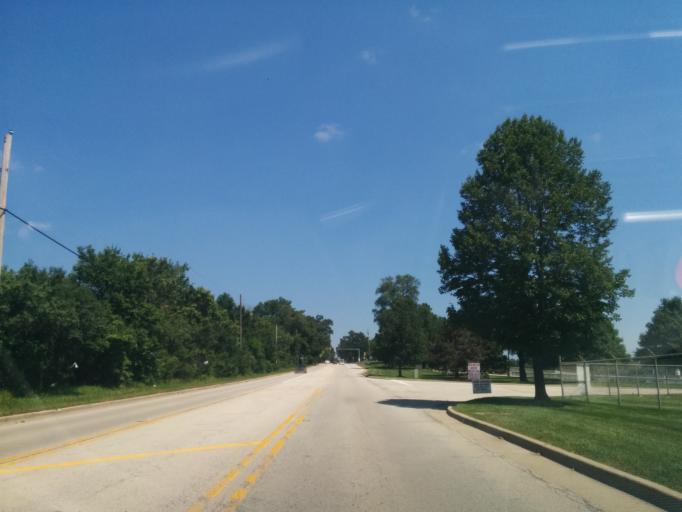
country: US
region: Illinois
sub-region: Cook County
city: Willow Springs
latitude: 41.7438
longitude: -87.8862
